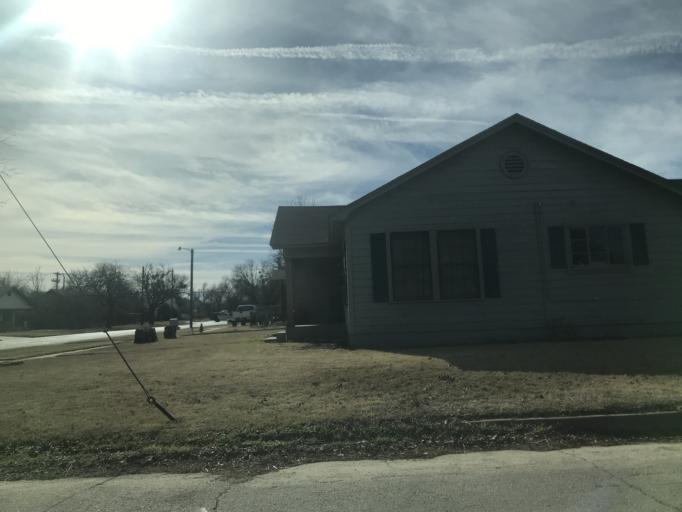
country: US
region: Texas
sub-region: Taylor County
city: Abilene
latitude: 32.4439
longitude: -99.7414
